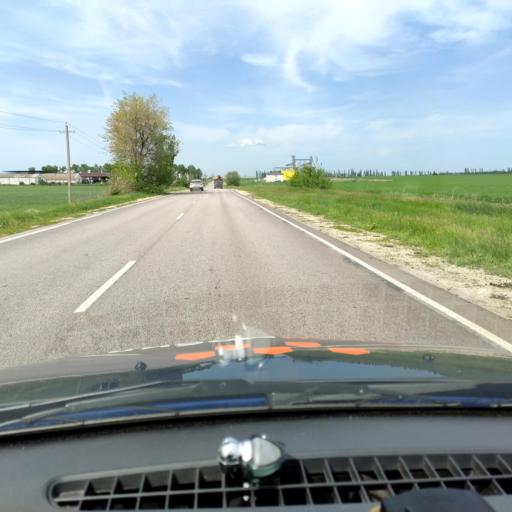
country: RU
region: Voronezj
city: Novaya Usman'
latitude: 51.5764
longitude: 39.3751
